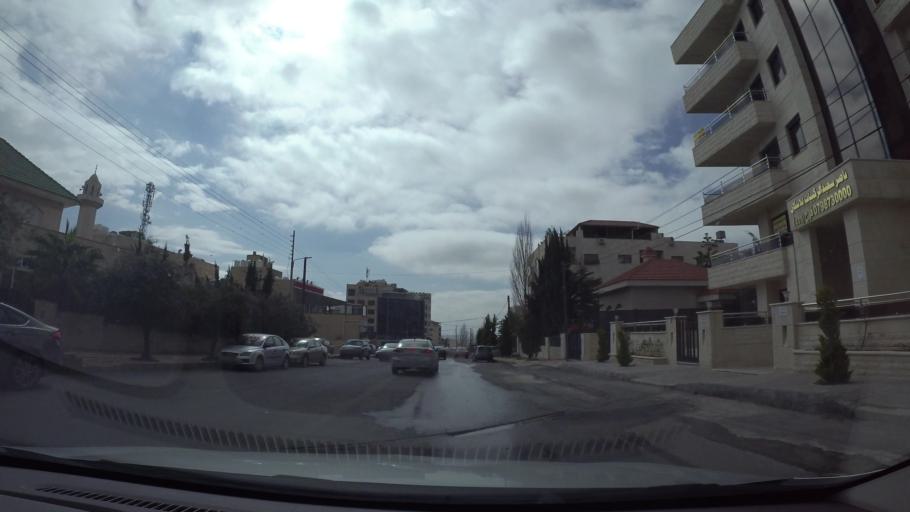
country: JO
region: Amman
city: Al Jubayhah
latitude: 31.9975
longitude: 35.8360
